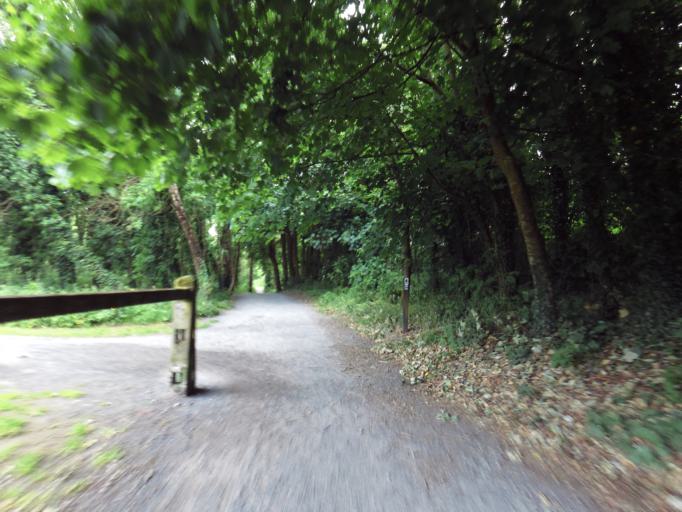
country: IE
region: Connaught
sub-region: County Galway
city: Gaillimh
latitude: 53.2949
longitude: -9.0804
